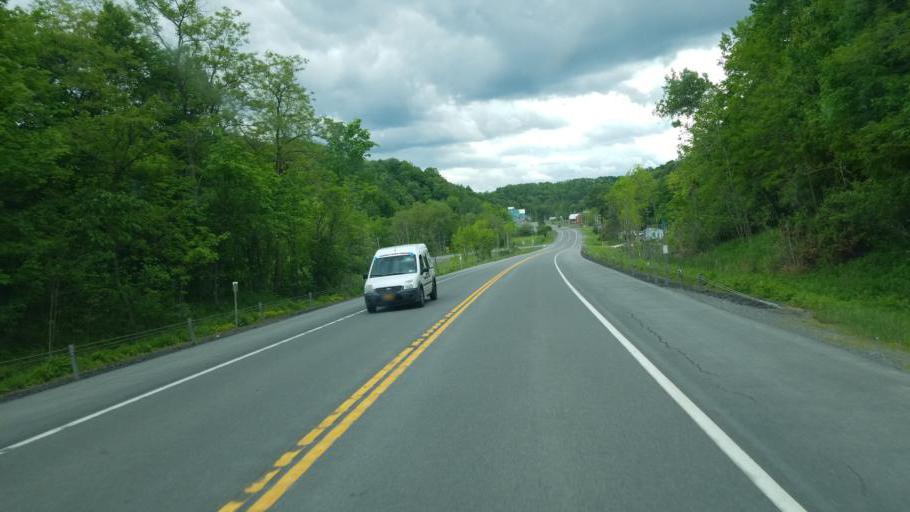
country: US
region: New York
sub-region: Oneida County
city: Chadwicks
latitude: 42.9628
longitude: -75.2469
